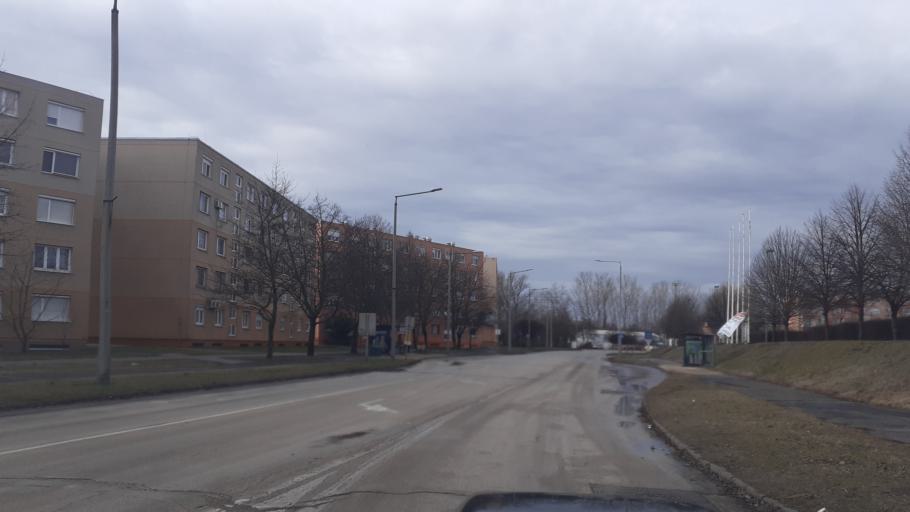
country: HU
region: Fejer
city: dunaujvaros
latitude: 46.9600
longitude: 18.9203
